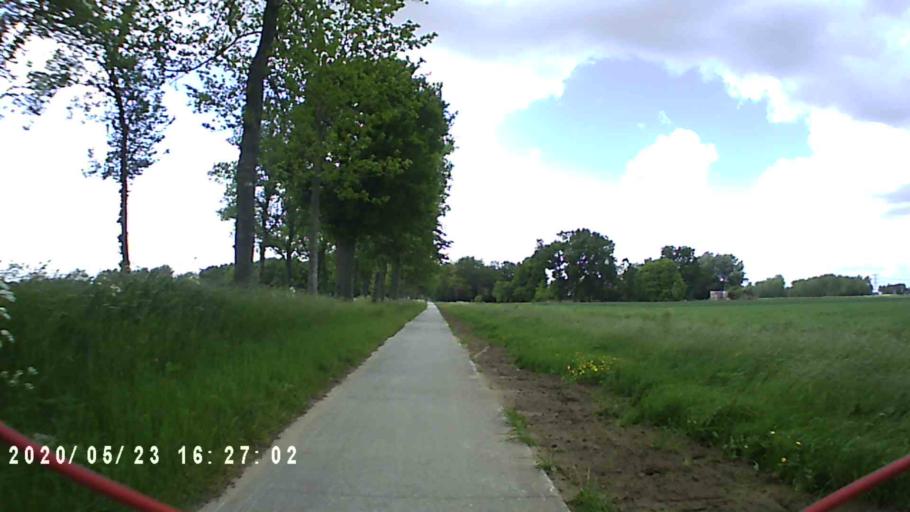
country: NL
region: Groningen
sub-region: Gemeente Appingedam
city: Appingedam
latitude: 53.2680
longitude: 6.8487
